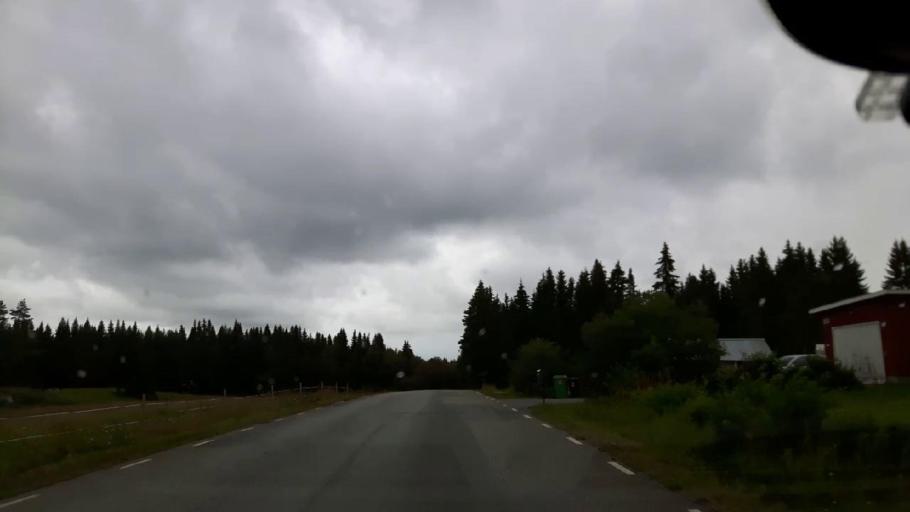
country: SE
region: Jaemtland
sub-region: OEstersunds Kommun
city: Ostersund
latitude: 63.0054
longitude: 14.5838
